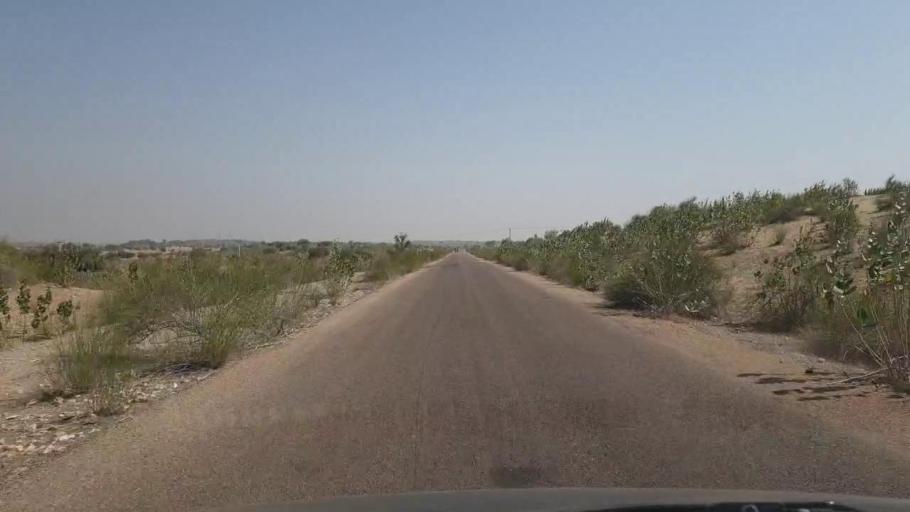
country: PK
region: Sindh
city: Chor
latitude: 25.6014
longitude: 70.0196
